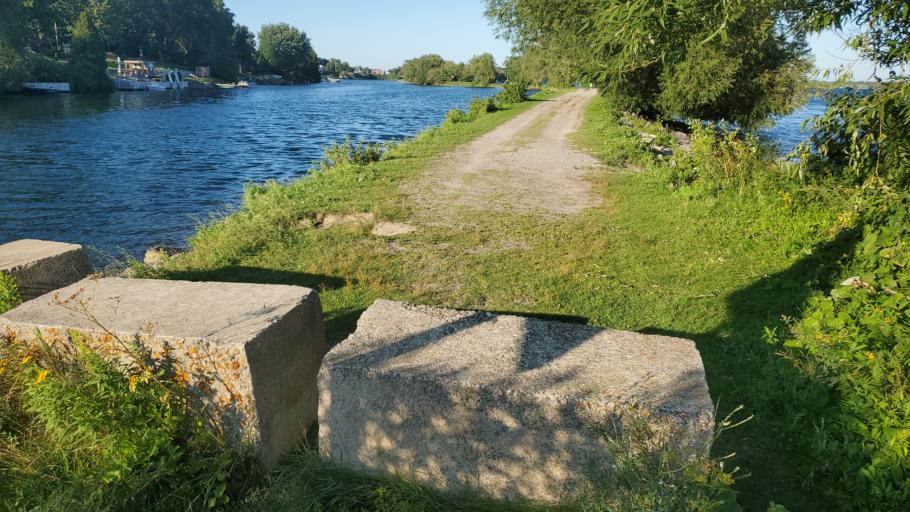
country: US
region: New York
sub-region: St. Lawrence County
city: Ogdensburg
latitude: 44.7784
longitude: -75.3960
